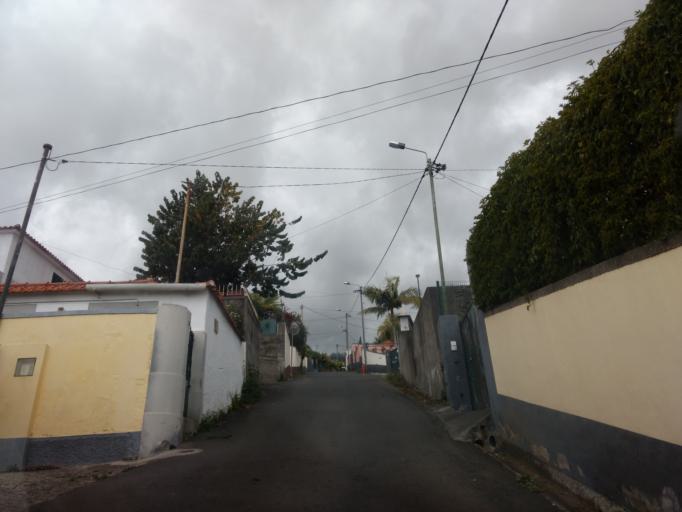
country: PT
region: Madeira
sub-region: Funchal
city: Nossa Senhora do Monte
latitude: 32.6673
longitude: -16.9351
